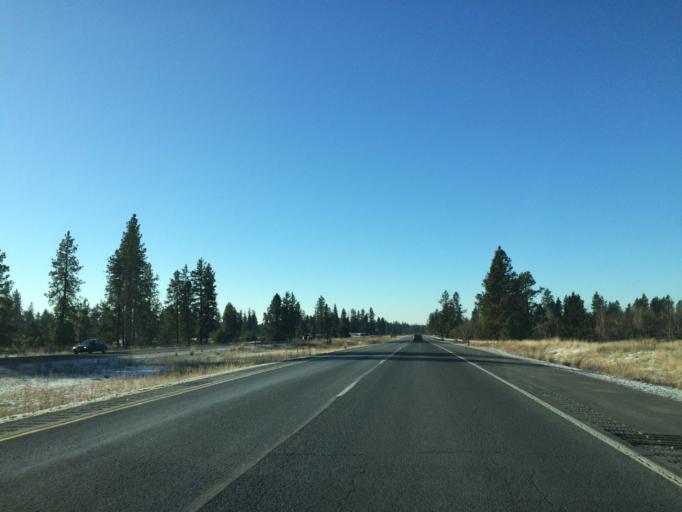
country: US
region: Washington
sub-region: Spokane County
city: Medical Lake
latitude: 47.5392
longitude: -117.6399
